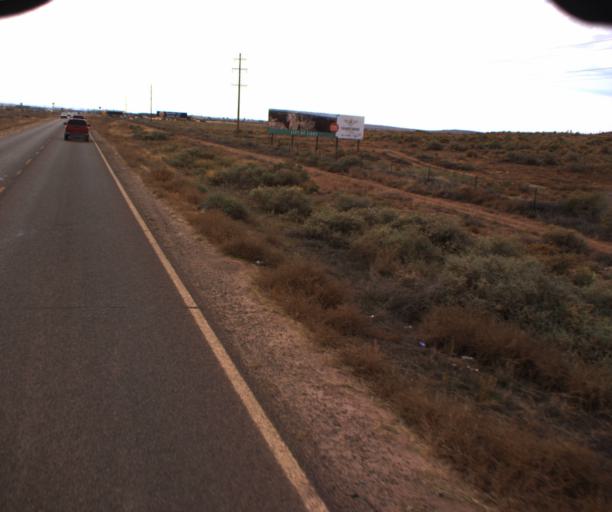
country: US
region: Arizona
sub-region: Apache County
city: Chinle
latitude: 36.1750
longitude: -109.5885
